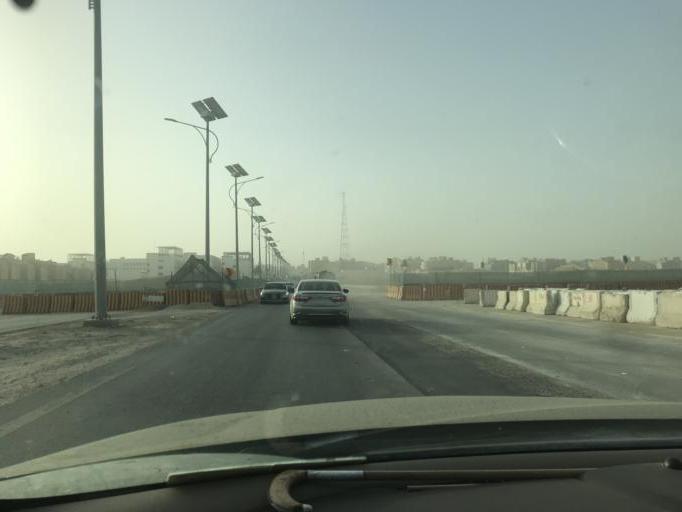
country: SA
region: Ar Riyad
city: Riyadh
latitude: 24.8457
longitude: 46.6642
